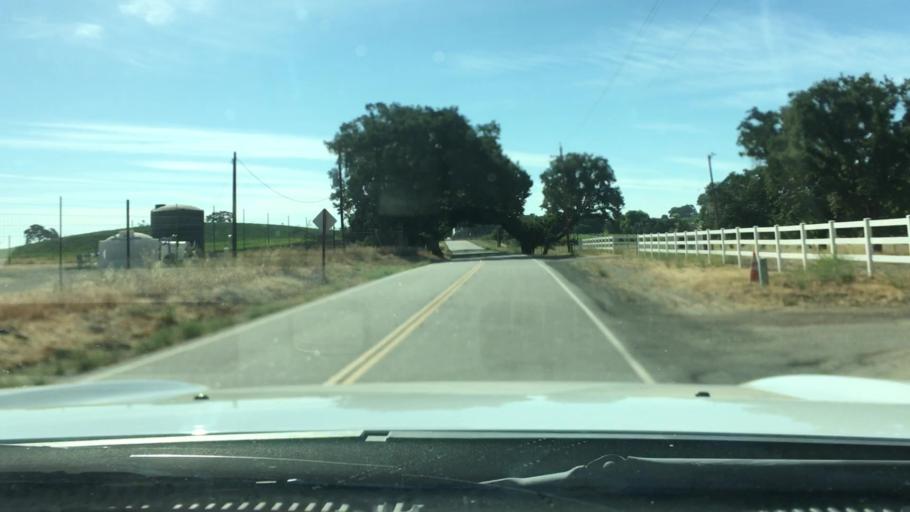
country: US
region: California
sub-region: San Luis Obispo County
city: Atascadero
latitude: 35.5556
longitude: -120.6242
